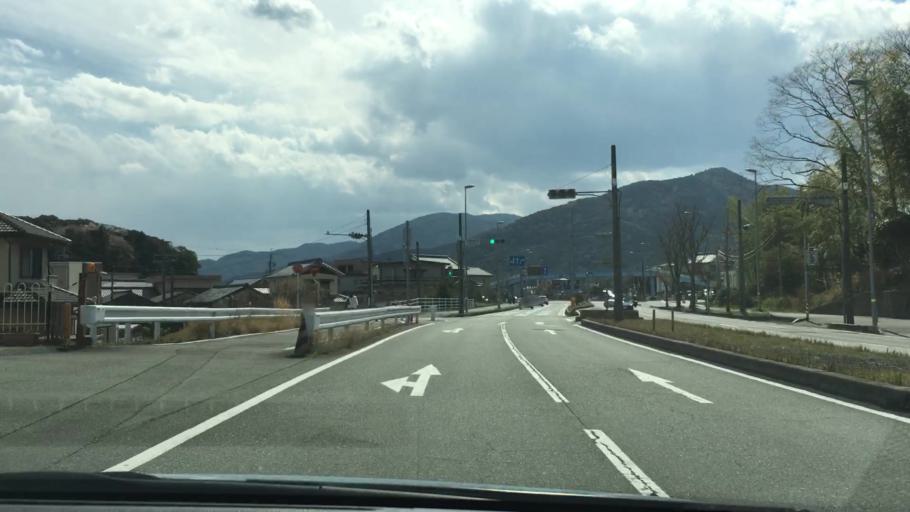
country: JP
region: Mie
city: Ise
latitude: 34.4719
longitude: 136.7292
